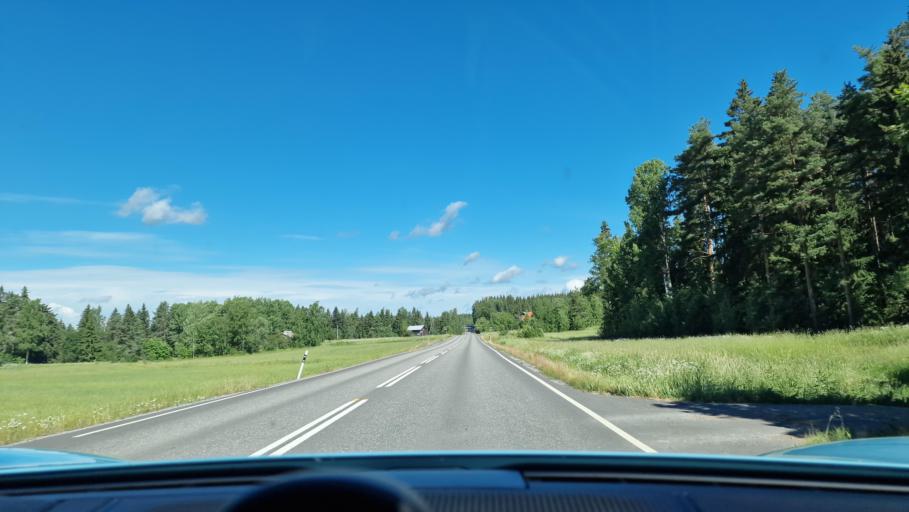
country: FI
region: Pirkanmaa
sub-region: Tampere
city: Sahalahti
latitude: 61.5669
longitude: 24.3057
